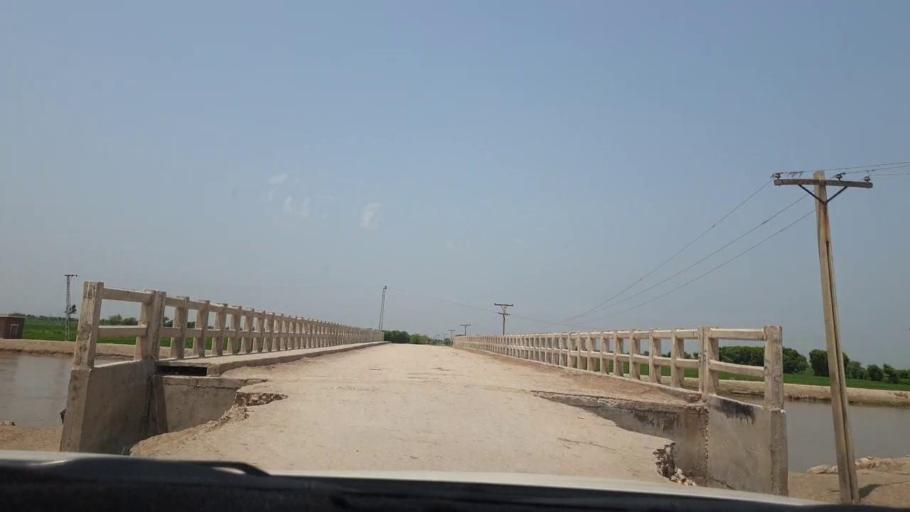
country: PK
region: Sindh
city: Radhan
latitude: 27.2470
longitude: 67.9865
